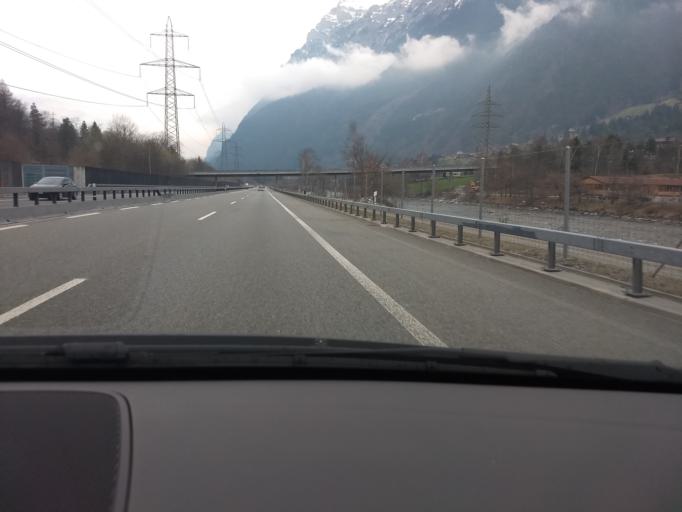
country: CH
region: Uri
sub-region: Uri
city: Silenen
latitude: 46.7928
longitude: 8.6655
